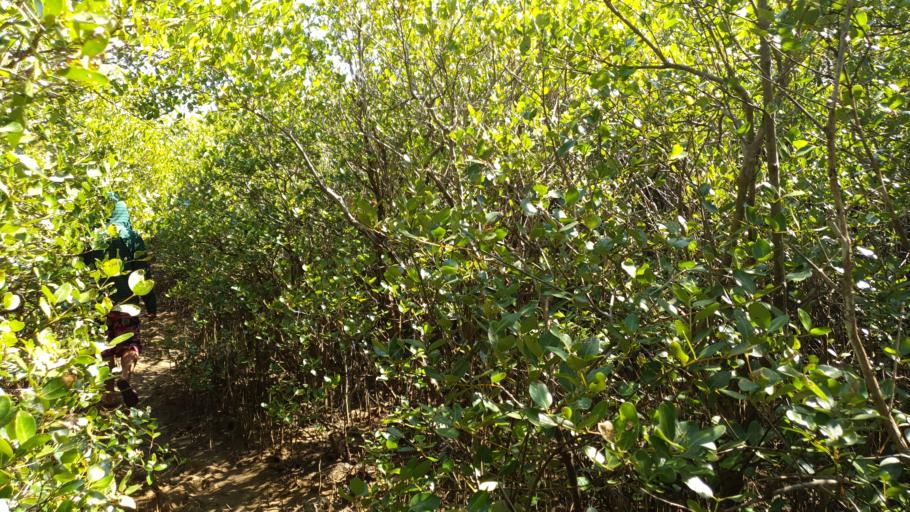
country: PH
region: Ilocos
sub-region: Province of La Union
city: Payocpoc Sur
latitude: 16.5044
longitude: 120.3092
